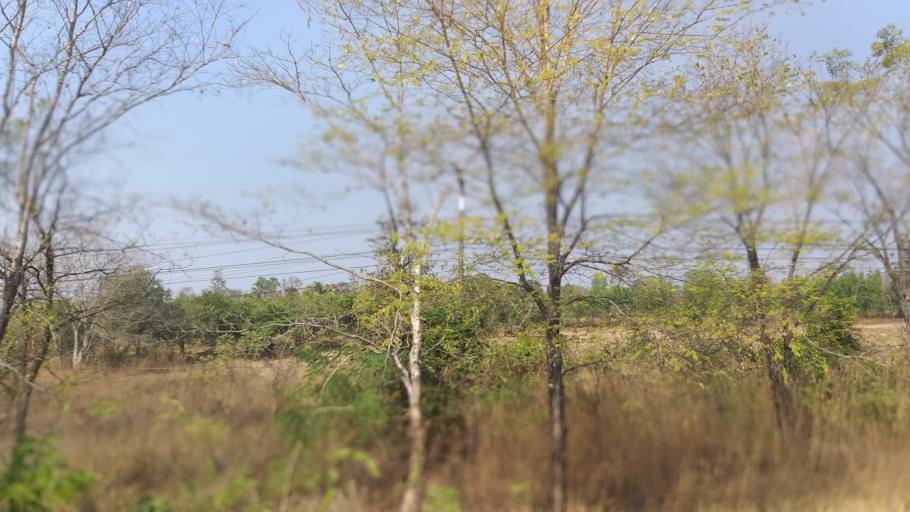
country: TH
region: Changwat Udon Thani
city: Nong Han
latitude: 17.3647
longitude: 103.0342
